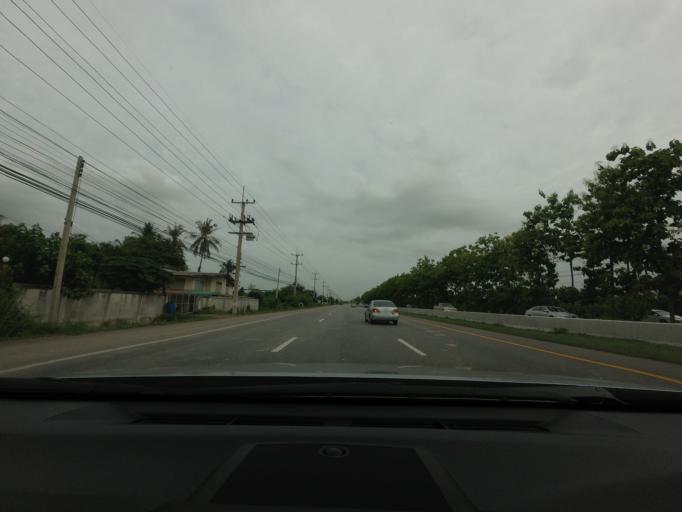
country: TH
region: Phetchaburi
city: Khao Yoi
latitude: 13.1905
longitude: 99.8329
